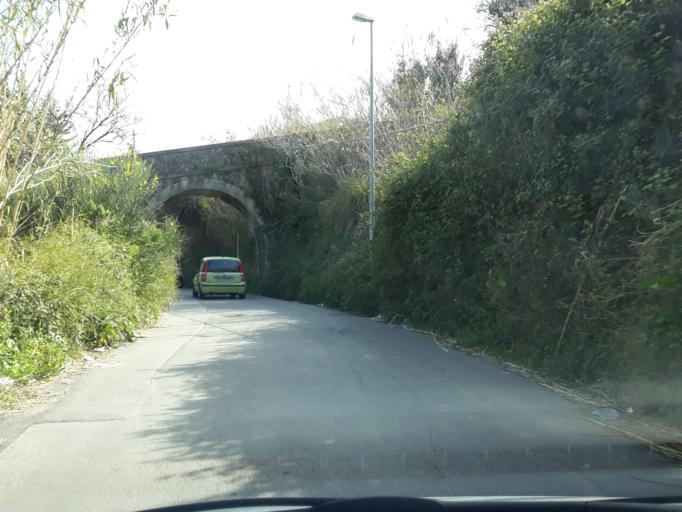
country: IT
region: Sicily
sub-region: Palermo
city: Monreale
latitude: 38.0733
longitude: 13.2826
